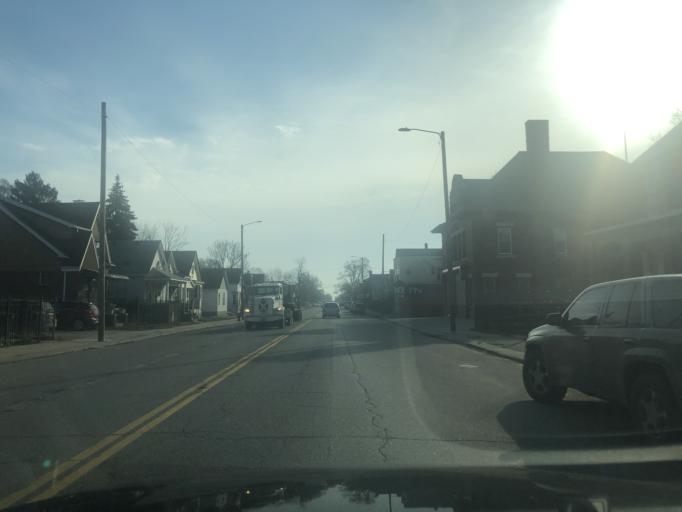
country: US
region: Michigan
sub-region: Wayne County
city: River Rouge
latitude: 42.3151
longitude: -83.1000
